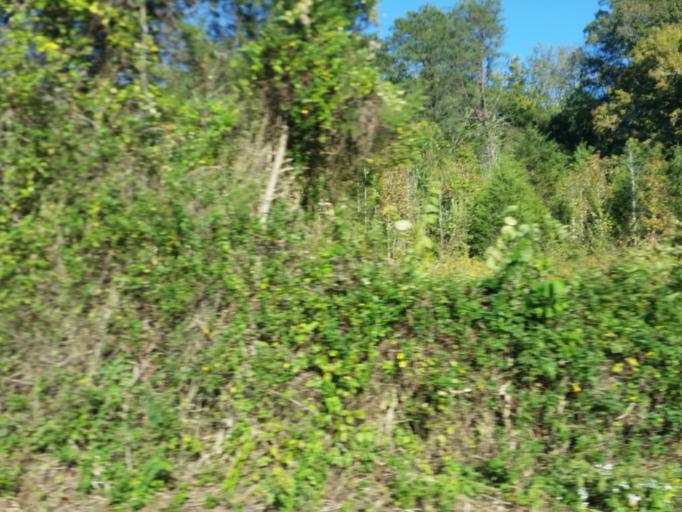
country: US
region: Tennessee
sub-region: Union County
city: Luttrell
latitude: 36.2523
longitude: -83.6522
